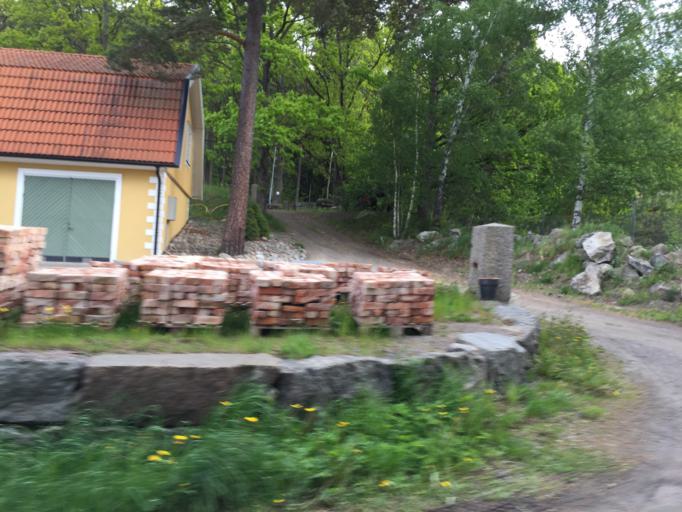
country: SE
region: OEstergoetland
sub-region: Finspangs Kommun
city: Finspang
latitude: 58.7095
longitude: 15.8524
